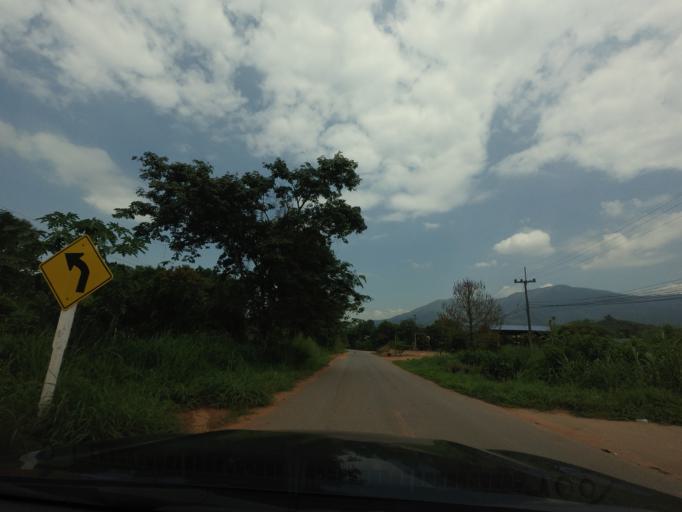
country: TH
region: Uttaradit
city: Fak Tha
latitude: 17.8152
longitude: 100.9379
